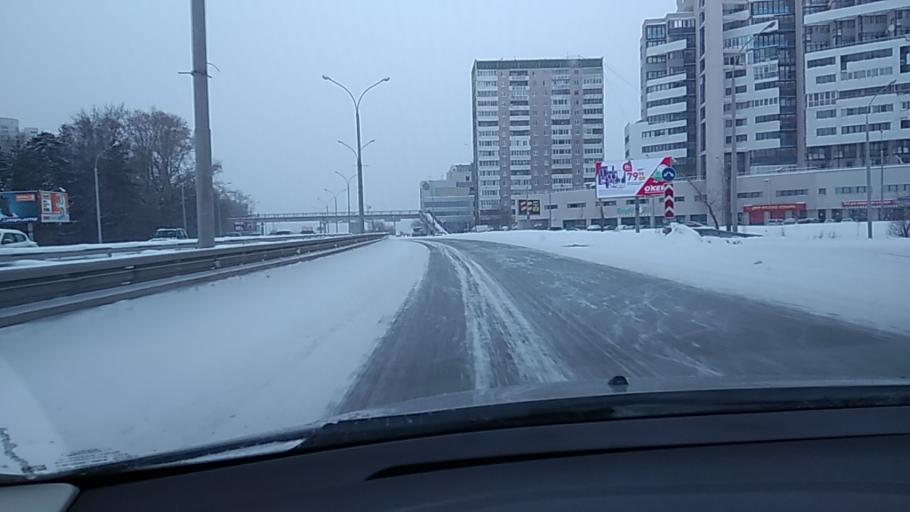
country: RU
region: Sverdlovsk
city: Yekaterinburg
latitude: 56.8257
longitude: 60.5602
